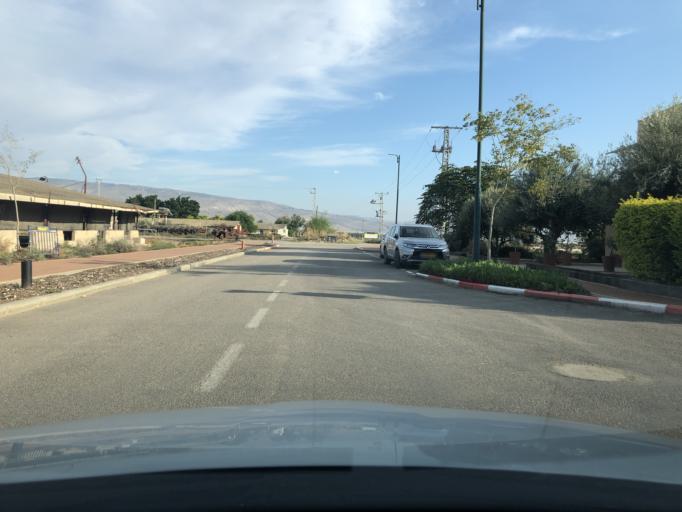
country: IL
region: Northern District
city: Yavne'el
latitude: 32.6561
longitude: 35.5784
